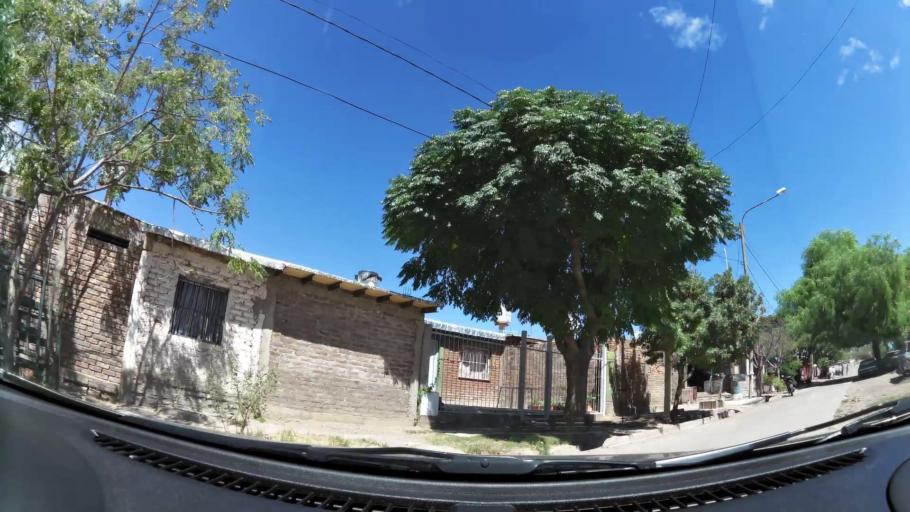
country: AR
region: Mendoza
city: Las Heras
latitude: -32.8623
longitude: -68.8642
